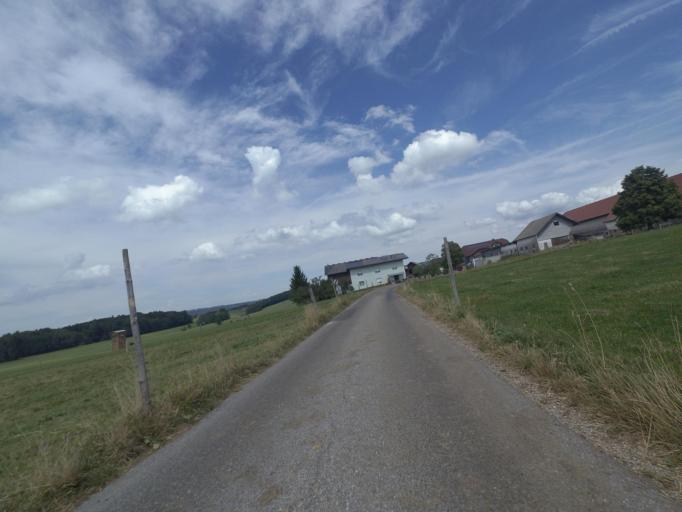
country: AT
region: Salzburg
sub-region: Politischer Bezirk Salzburg-Umgebung
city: Obertrum am See
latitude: 47.9111
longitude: 13.0923
